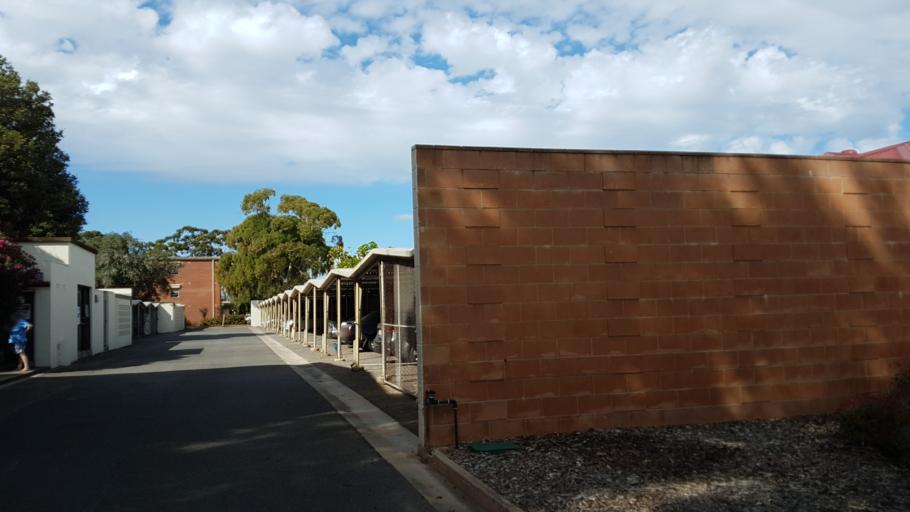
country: AU
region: South Australia
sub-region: City of West Torrens
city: Thebarton
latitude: -34.9259
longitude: 138.5496
